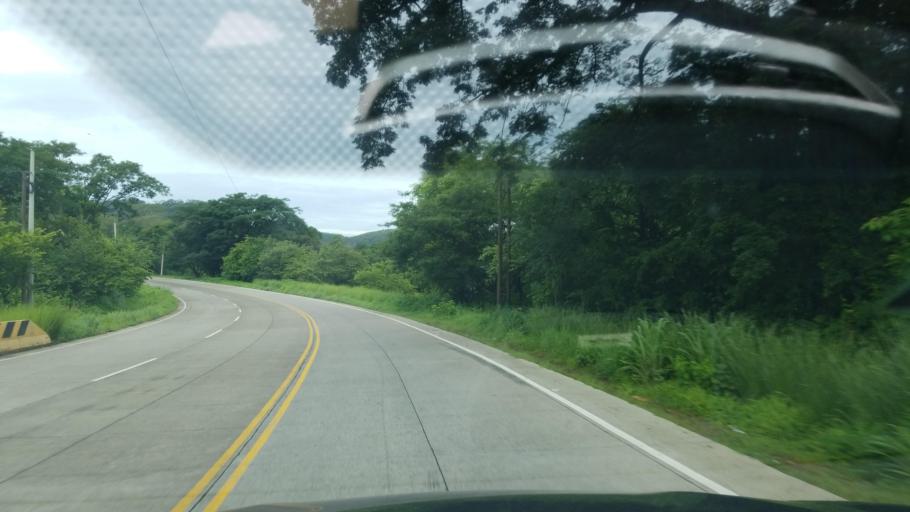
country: HN
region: Francisco Morazan
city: El Porvenir
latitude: 13.6947
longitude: -87.3280
